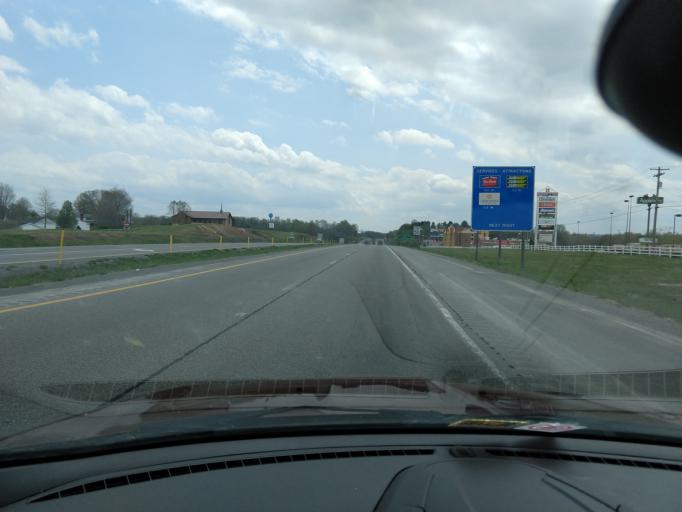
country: US
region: West Virginia
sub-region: Nicholas County
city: Summersville
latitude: 38.3013
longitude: -80.8336
